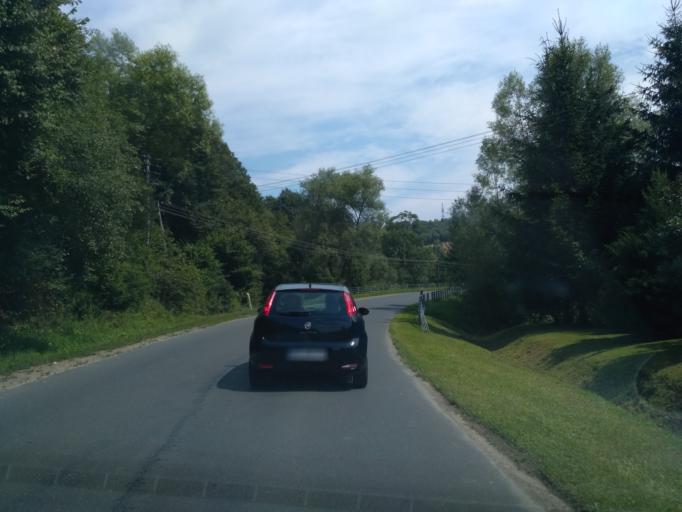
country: PL
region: Subcarpathian Voivodeship
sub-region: Powiat bieszczadzki
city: Czarna
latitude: 49.3001
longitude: 22.5565
